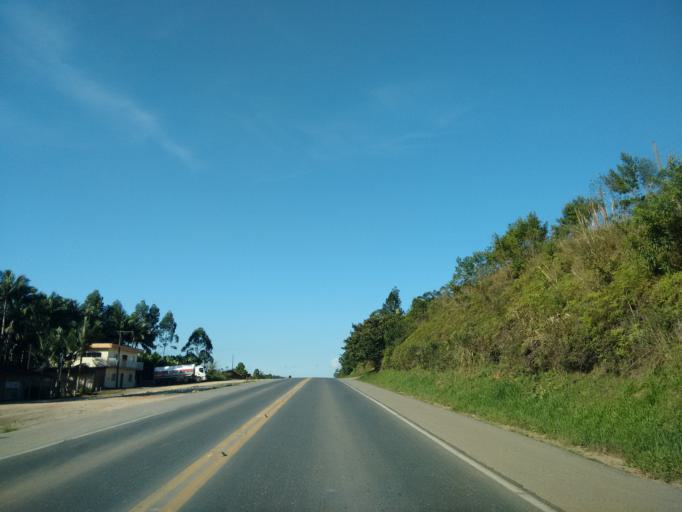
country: BR
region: Santa Catarina
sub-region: Guaramirim
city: Guaramirim
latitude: -26.4534
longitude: -48.9141
